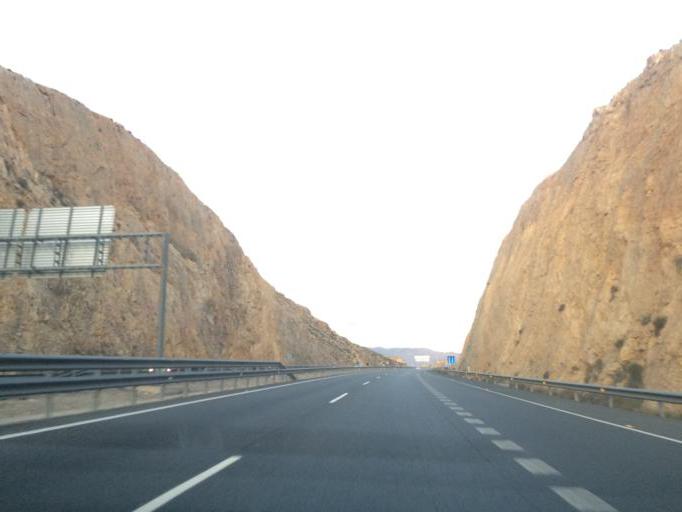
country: ES
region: Andalusia
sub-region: Provincia de Almeria
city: Almeria
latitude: 36.8581
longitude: -2.4708
